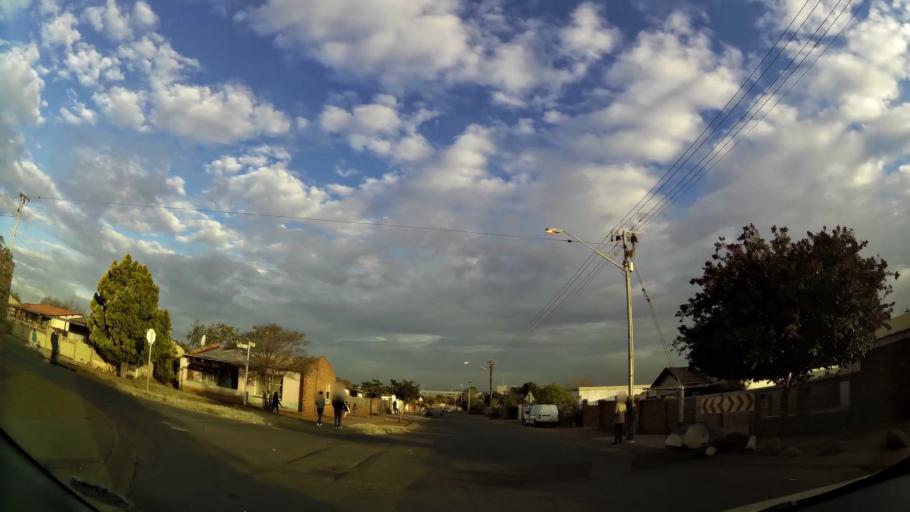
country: ZA
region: Gauteng
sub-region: City of Tshwane Metropolitan Municipality
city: Pretoria
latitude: -25.7079
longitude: 28.3205
